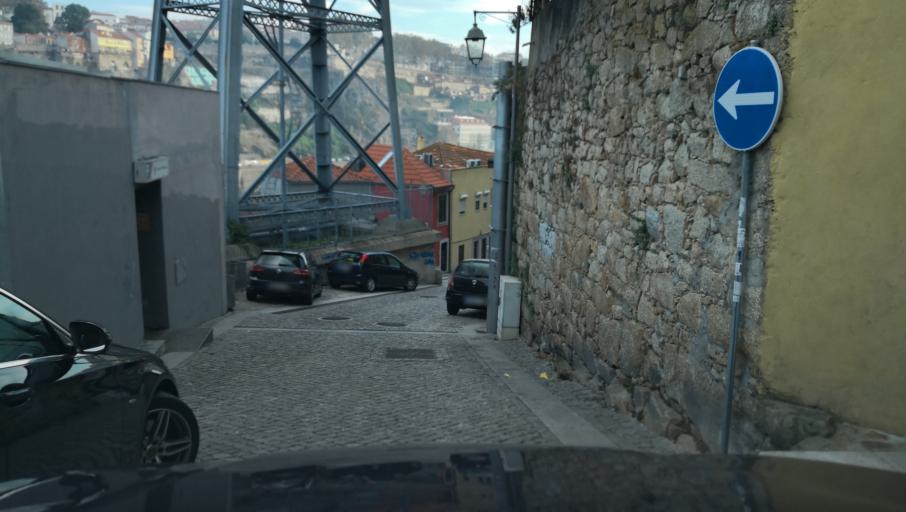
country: PT
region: Porto
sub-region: Vila Nova de Gaia
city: Vila Nova de Gaia
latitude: 41.1384
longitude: -8.6093
